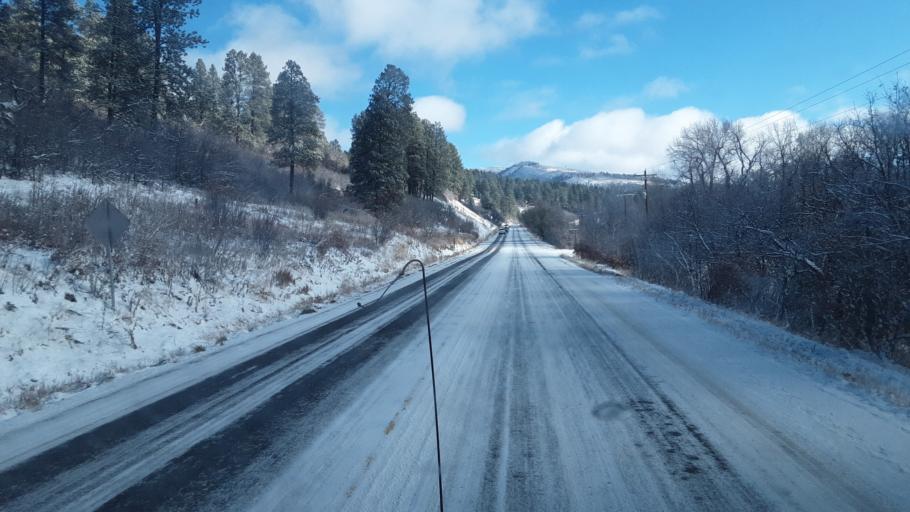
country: US
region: Colorado
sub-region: La Plata County
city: Bayfield
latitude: 37.3505
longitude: -107.6947
